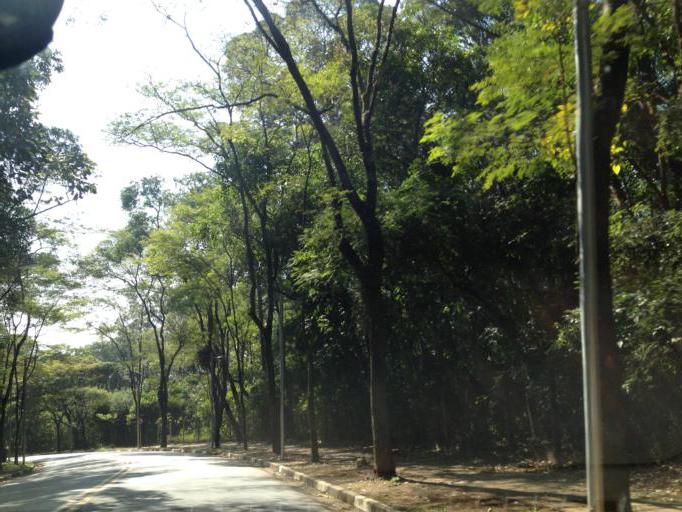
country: BR
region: Sao Paulo
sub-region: Osasco
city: Osasco
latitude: -23.5630
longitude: -46.7291
